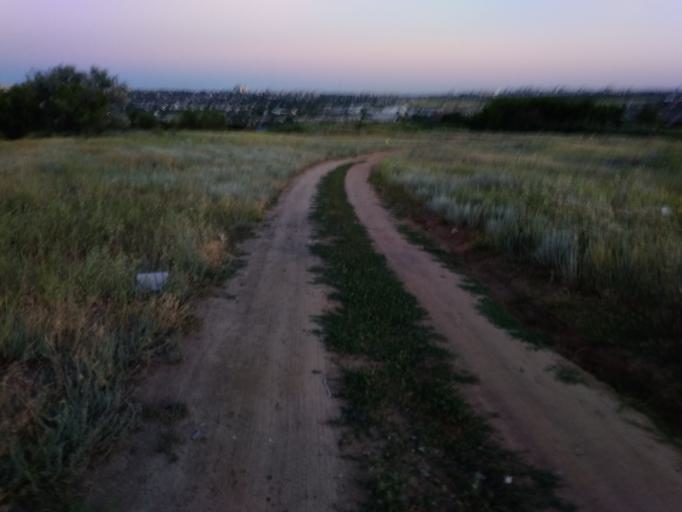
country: RU
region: Volgograd
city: Vodstroy
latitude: 48.8047
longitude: 44.5378
